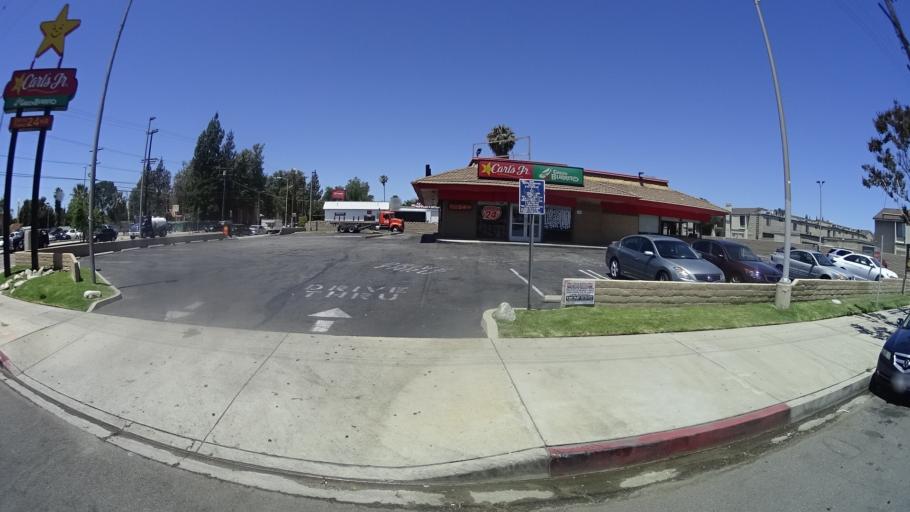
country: US
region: California
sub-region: Los Angeles County
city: San Fernando
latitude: 34.2432
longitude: -118.4677
